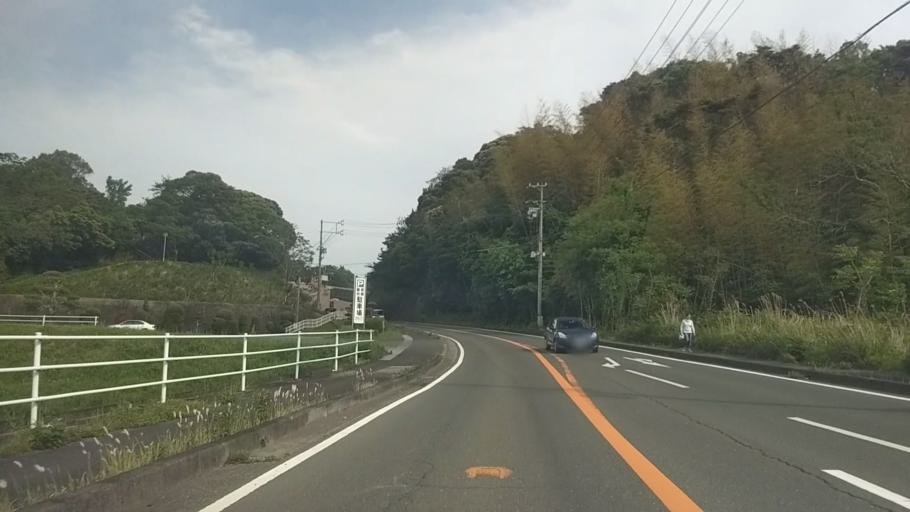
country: JP
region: Shizuoka
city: Hamamatsu
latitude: 34.7076
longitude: 137.6340
